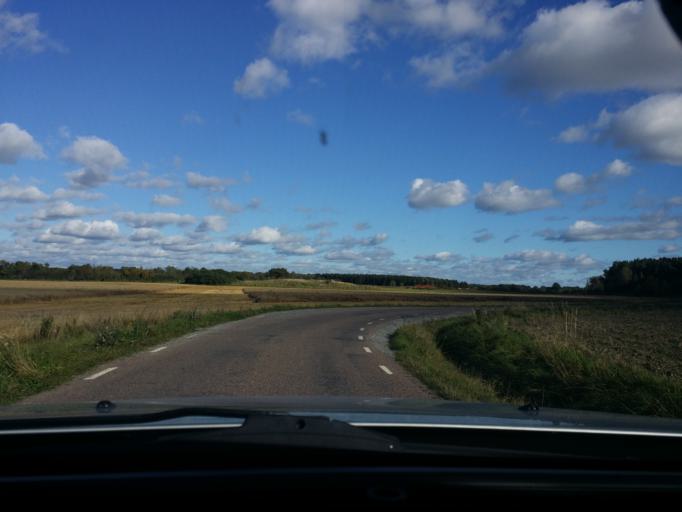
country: SE
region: Vaestmanland
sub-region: Vasteras
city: Vasteras
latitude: 59.5385
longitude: 16.4712
